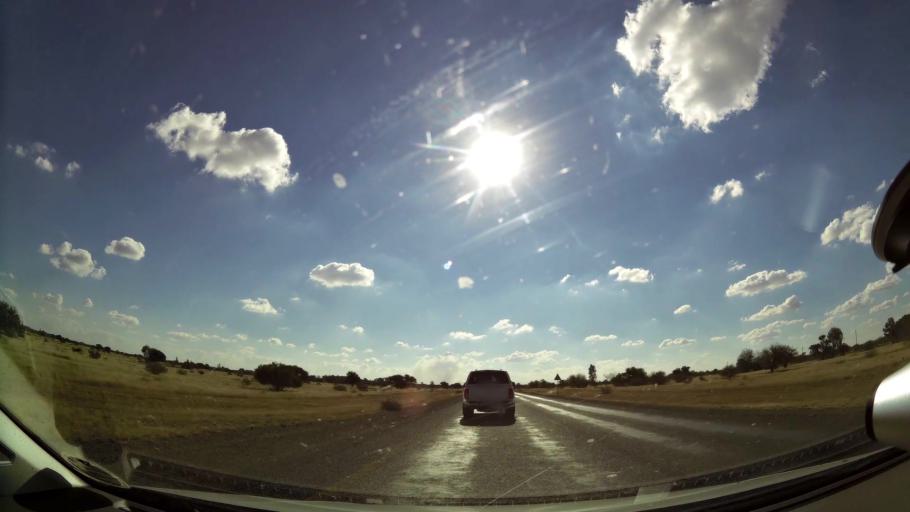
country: ZA
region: Northern Cape
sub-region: Frances Baard District Municipality
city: Kimberley
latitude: -28.8000
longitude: 24.7927
